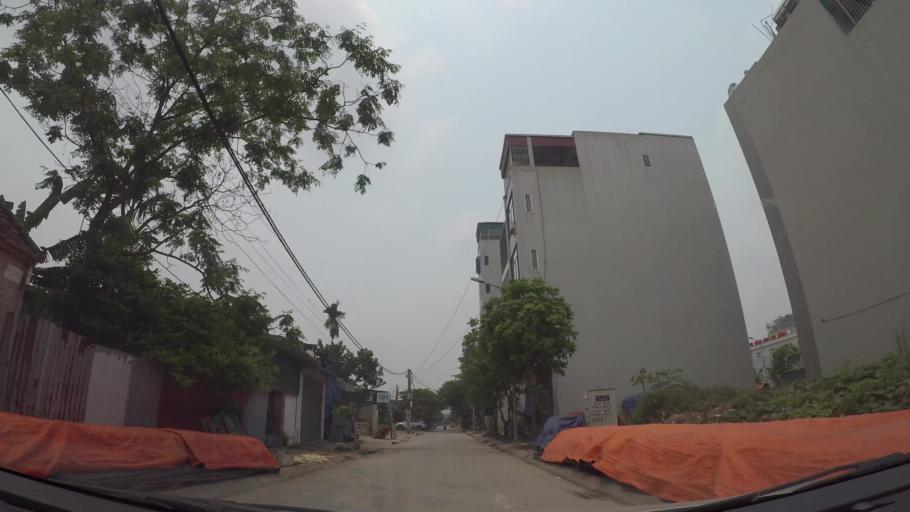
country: VN
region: Ha Noi
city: Ha Dong
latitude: 20.9888
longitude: 105.7432
